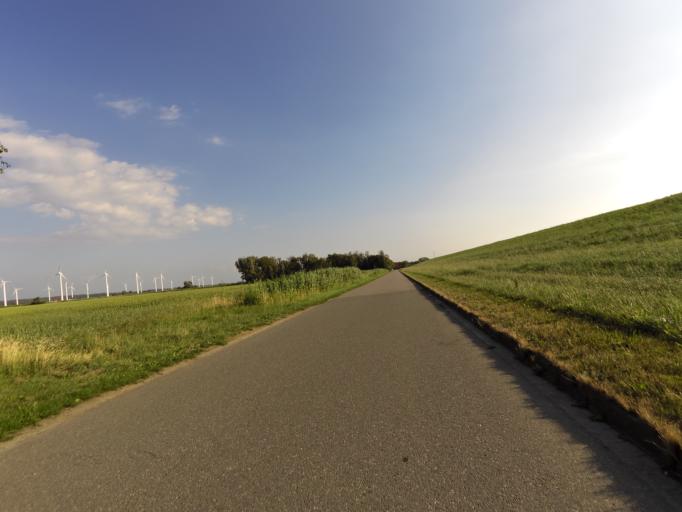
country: DE
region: Lower Saxony
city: Nordholz
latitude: 53.8039
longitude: 8.5694
